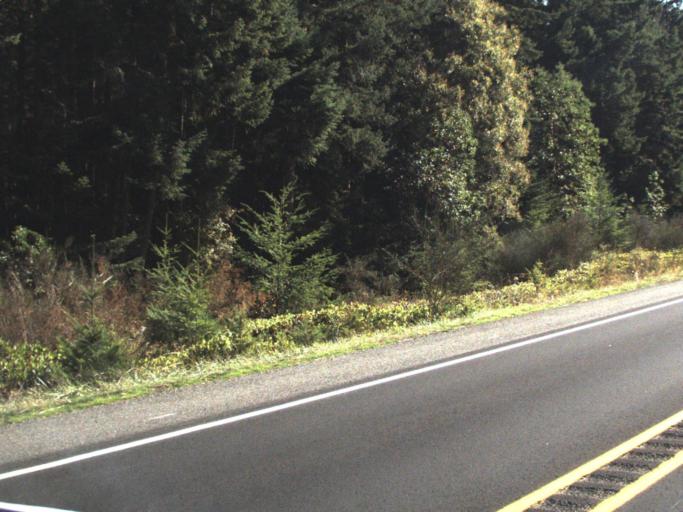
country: US
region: Washington
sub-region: Island County
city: Coupeville
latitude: 48.2290
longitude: -122.7399
